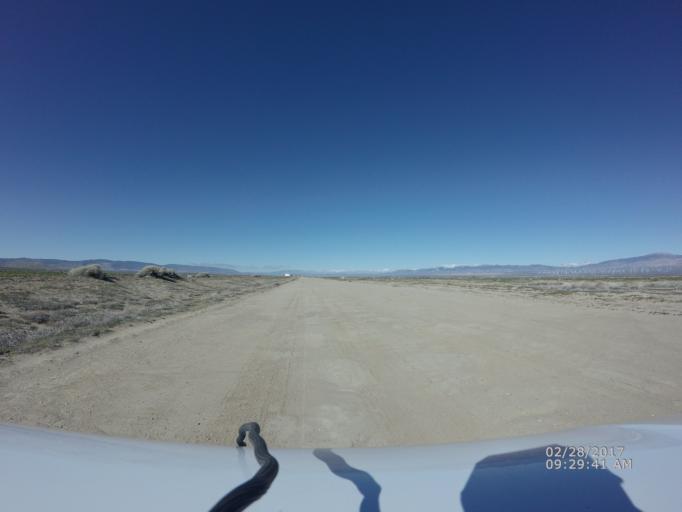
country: US
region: California
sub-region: Los Angeles County
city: Green Valley
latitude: 34.8049
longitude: -118.3499
